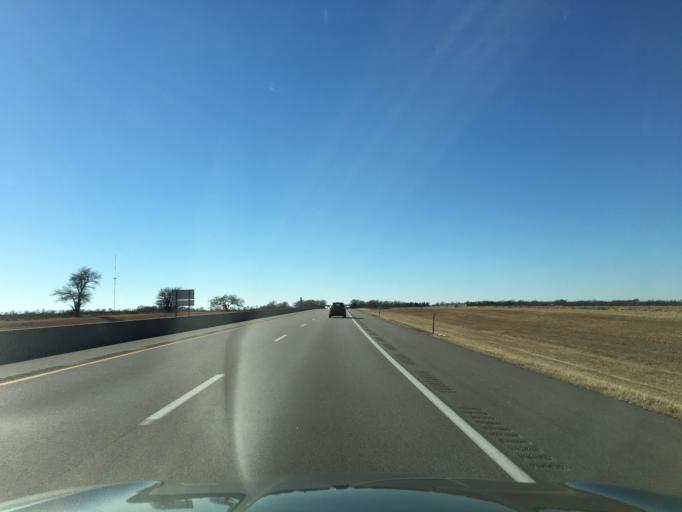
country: US
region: Kansas
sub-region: Sumner County
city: Belle Plaine
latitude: 37.3407
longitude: -97.3250
